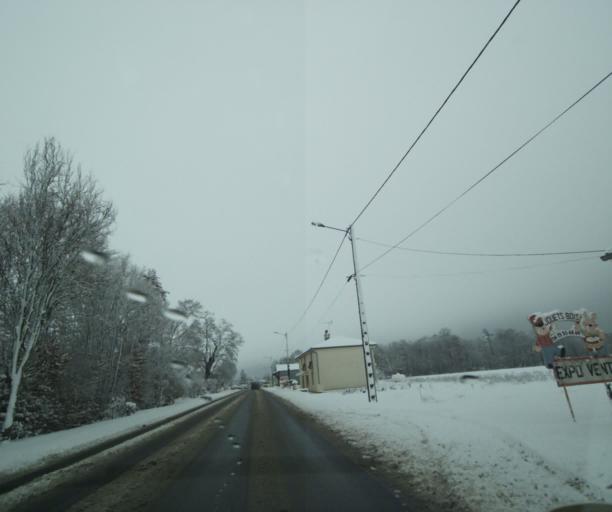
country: FR
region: Champagne-Ardenne
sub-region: Departement de la Haute-Marne
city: Wassy
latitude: 48.5444
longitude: 4.9235
